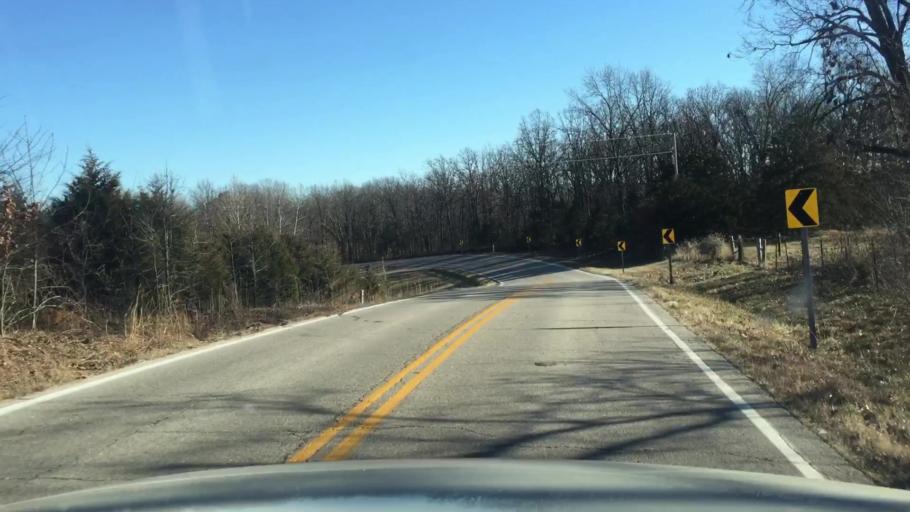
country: US
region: Missouri
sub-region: Morgan County
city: Versailles
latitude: 38.3436
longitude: -92.7324
